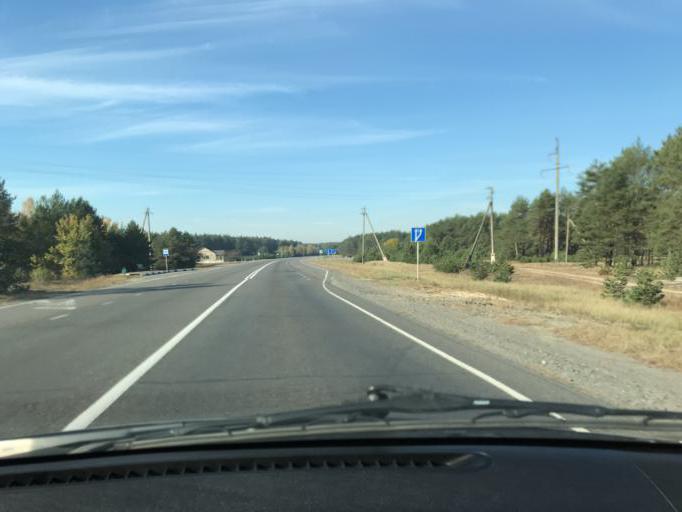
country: BY
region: Brest
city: Davyd-Haradok
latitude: 52.2356
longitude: 27.2461
